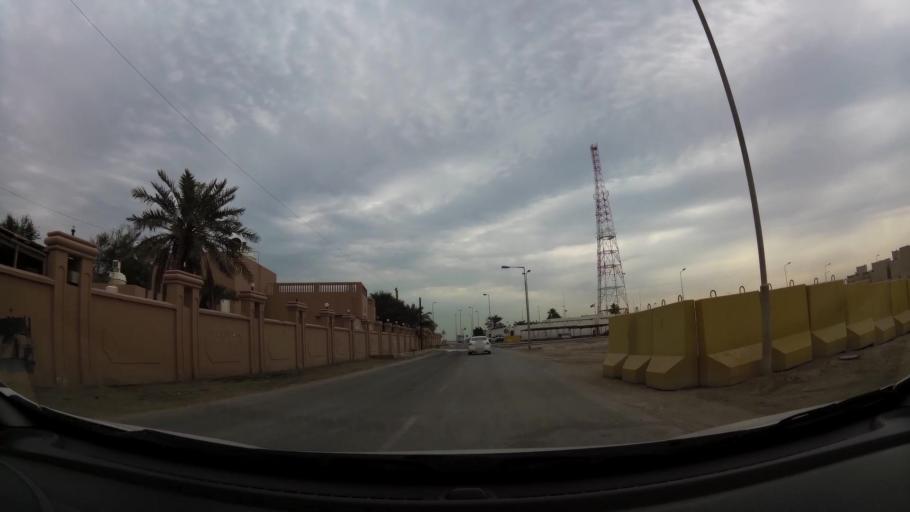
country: BH
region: Manama
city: Manama
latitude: 26.1833
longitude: 50.5876
